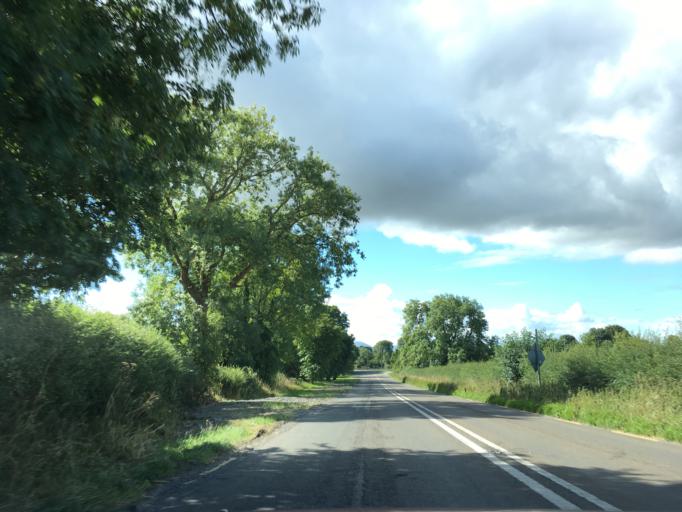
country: IE
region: Munster
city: Cahir
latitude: 52.4306
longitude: -7.8863
